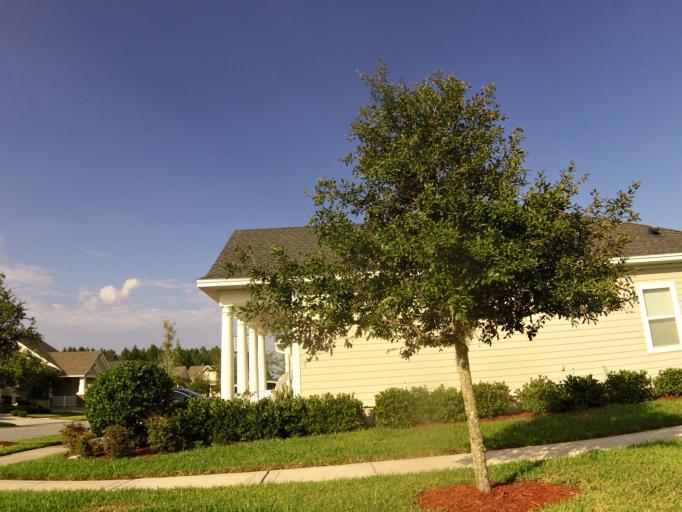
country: US
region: Florida
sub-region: Clay County
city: Green Cove Springs
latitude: 30.0254
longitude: -81.6364
